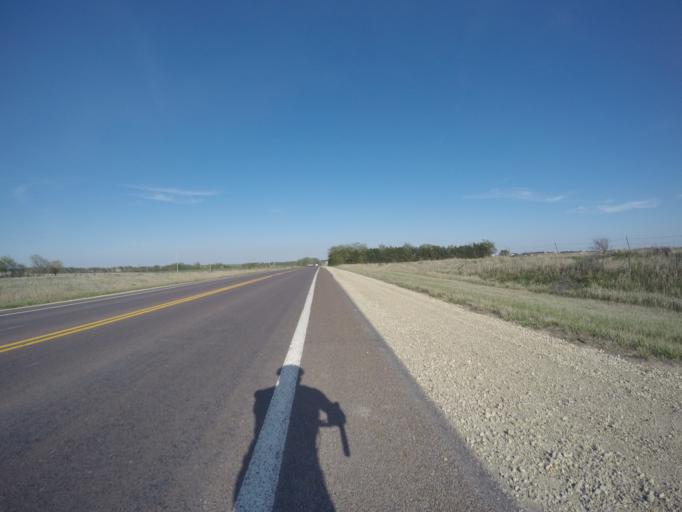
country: US
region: Kansas
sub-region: Riley County
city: Fort Riley North
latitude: 39.2985
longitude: -96.7870
